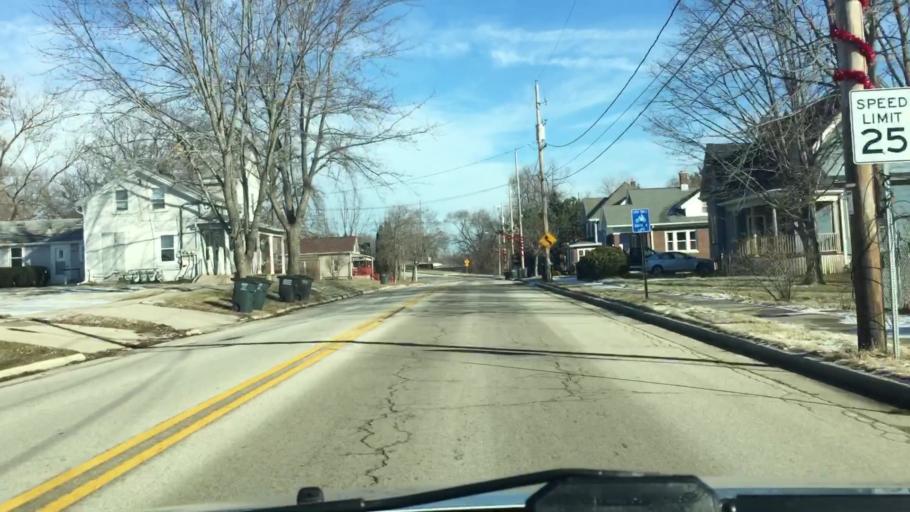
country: US
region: Wisconsin
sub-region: Waukesha County
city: Mukwonago
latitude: 42.8638
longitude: -88.3313
